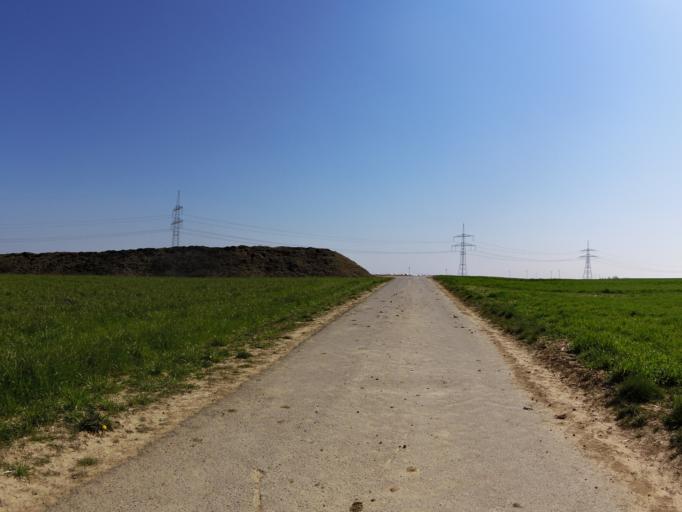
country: DE
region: Bavaria
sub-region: Regierungsbezirk Unterfranken
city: Rottendorf
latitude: 49.8225
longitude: 10.0802
